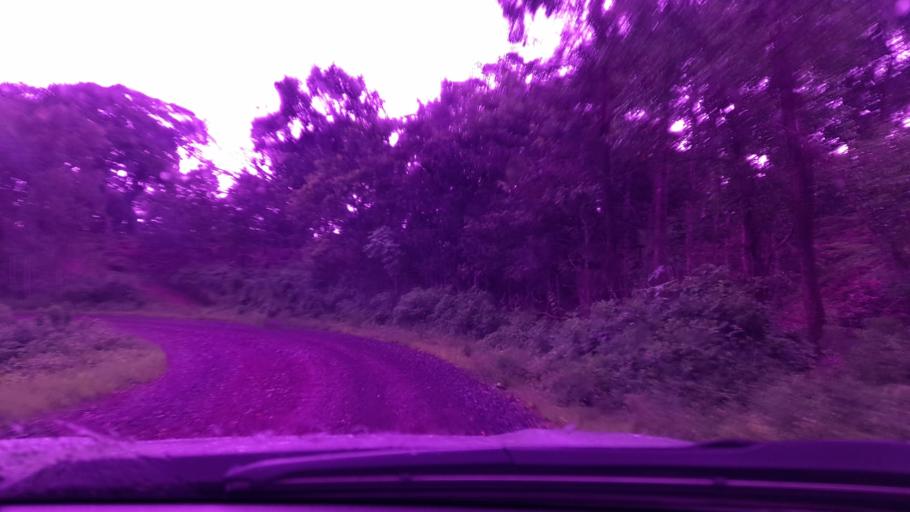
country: ET
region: Oromiya
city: Metu
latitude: 8.4510
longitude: 35.6339
